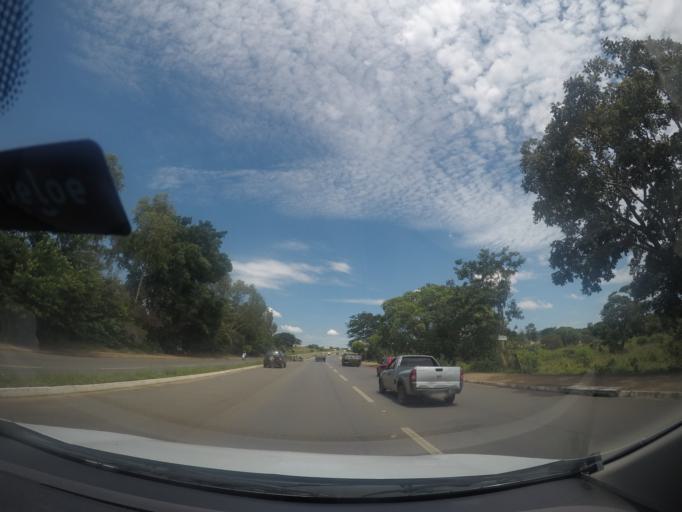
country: BR
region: Goias
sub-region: Goiania
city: Goiania
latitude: -16.6838
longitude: -49.3387
